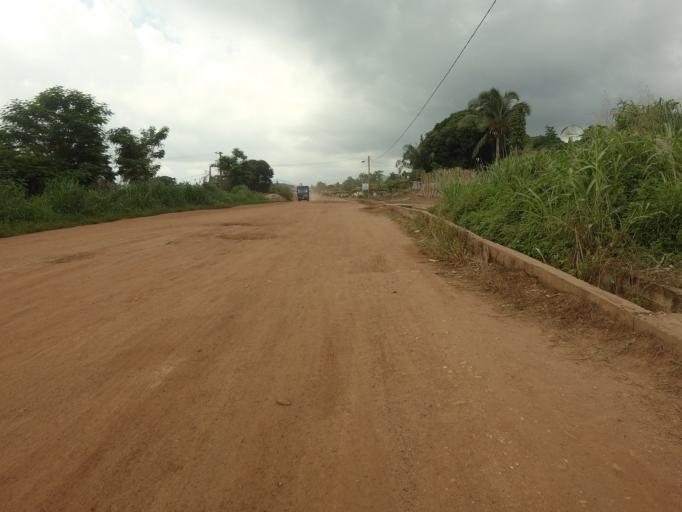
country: TG
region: Plateaux
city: Kpalime
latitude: 6.9180
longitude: 0.4592
